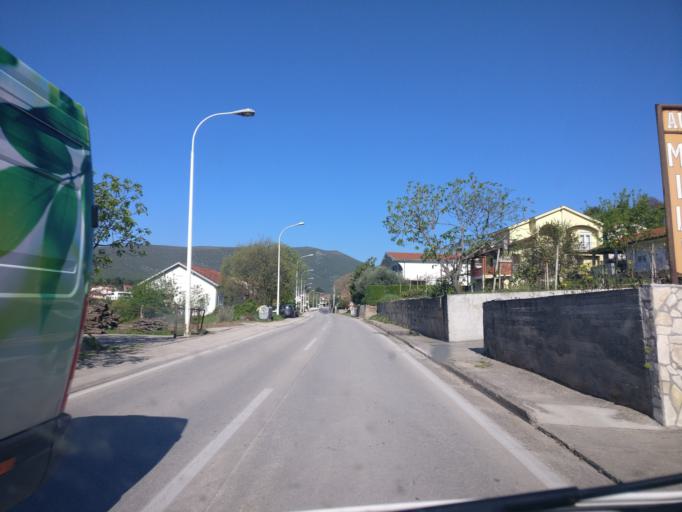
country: BA
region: Federation of Bosnia and Herzegovina
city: Capljina
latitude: 43.1179
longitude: 17.6946
